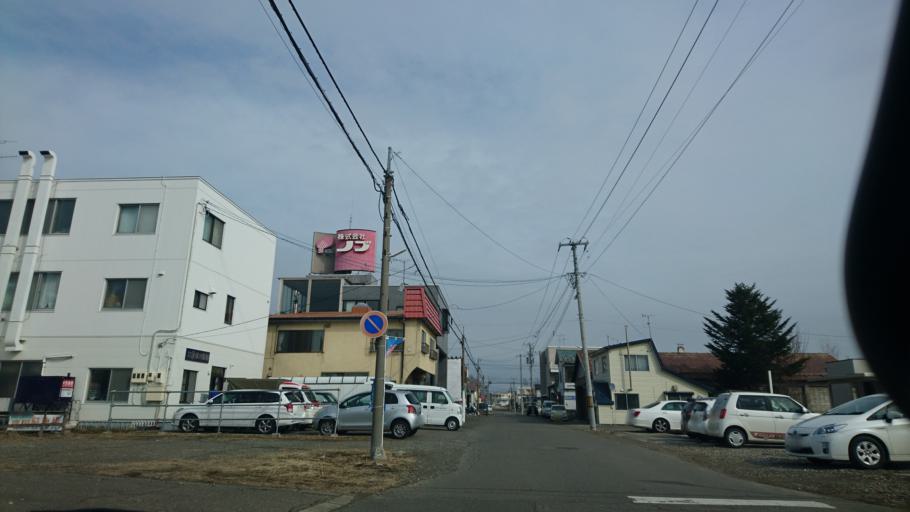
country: JP
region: Hokkaido
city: Obihiro
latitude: 42.9274
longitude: 143.2055
